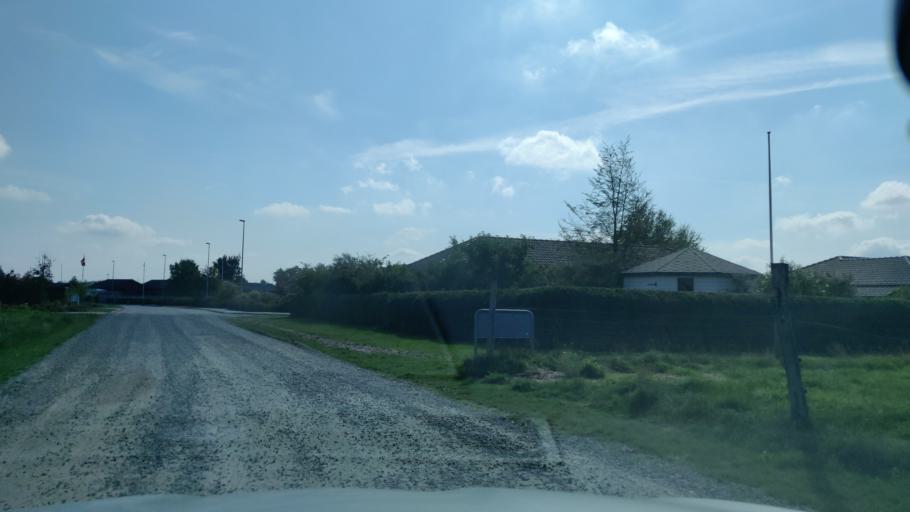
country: DK
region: Central Jutland
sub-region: Herning Kommune
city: Avlum
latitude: 56.2176
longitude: 8.8500
